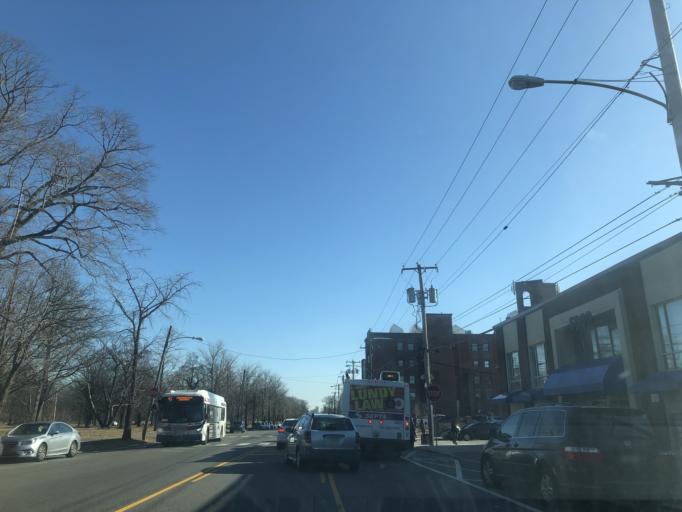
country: US
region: Pennsylvania
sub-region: Montgomery County
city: Bala-Cynwyd
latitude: 39.9801
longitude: -75.2199
